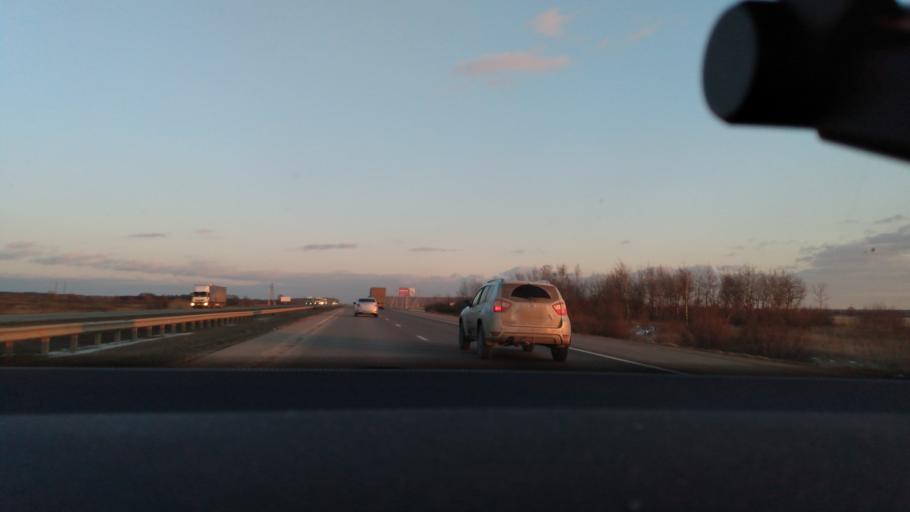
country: RU
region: Moskovskaya
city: Kolomna
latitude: 55.1141
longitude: 38.8522
